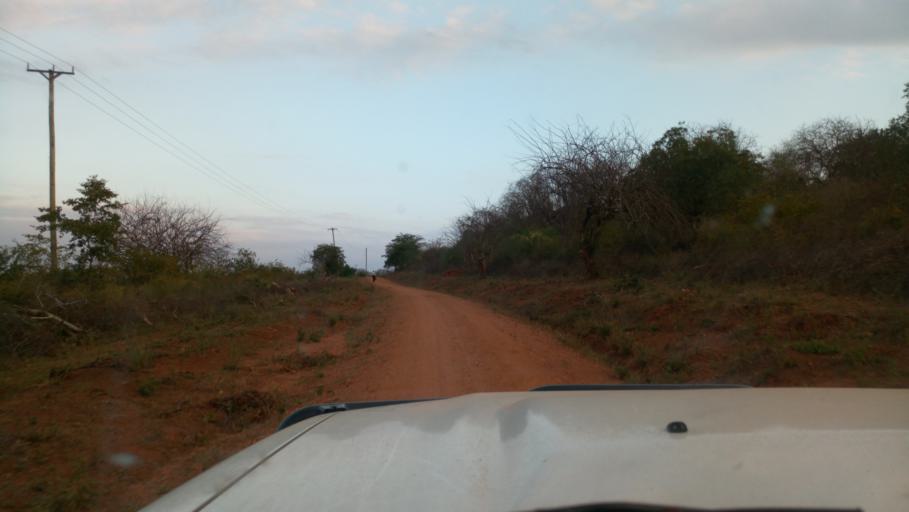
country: KE
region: Kitui
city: Kitui
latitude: -1.7081
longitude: 38.2438
